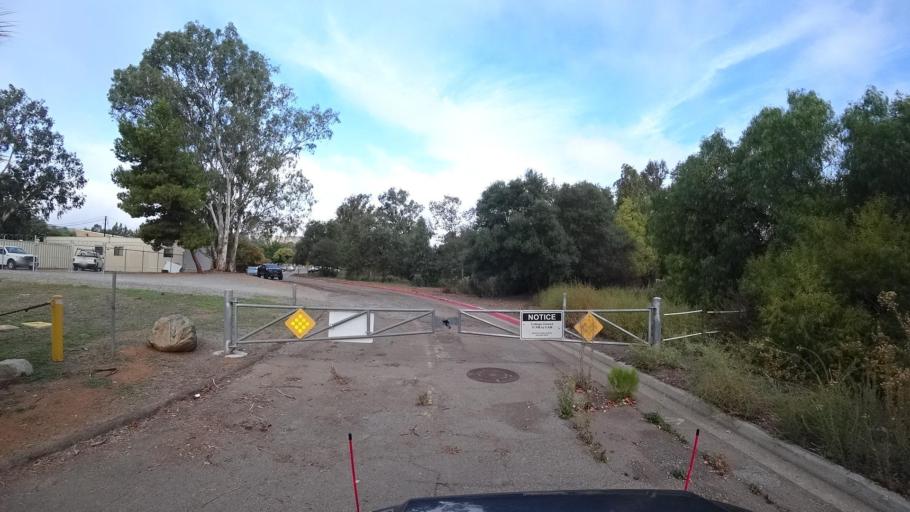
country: US
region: California
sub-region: San Diego County
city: Rancho San Diego
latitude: 32.7432
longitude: -116.9372
